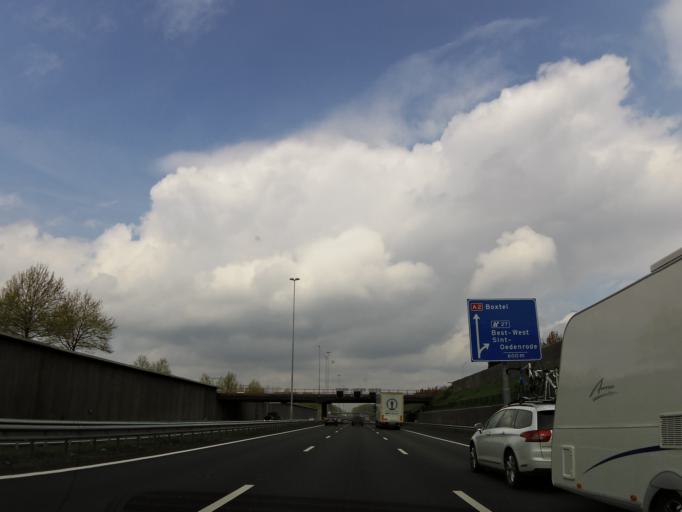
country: NL
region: North Brabant
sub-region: Gemeente Best
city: Best
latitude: 51.5153
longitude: 5.4020
